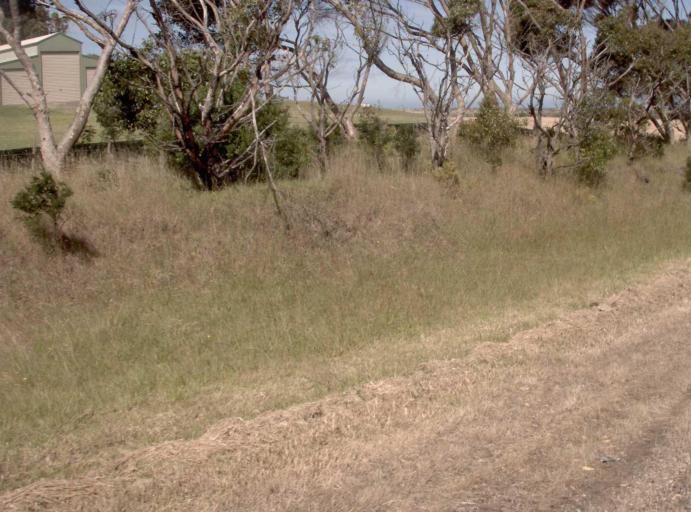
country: AU
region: Victoria
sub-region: Wellington
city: Sale
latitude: -38.3621
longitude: 147.1814
